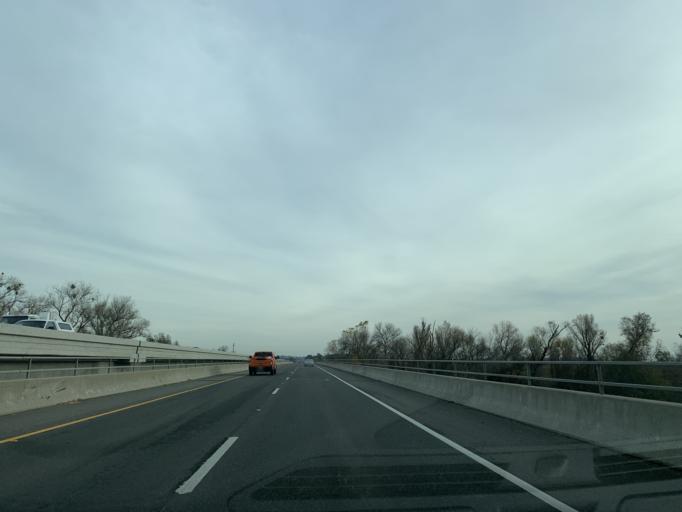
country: US
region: California
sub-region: Yuba County
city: Plumas Lake
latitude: 38.9013
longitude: -121.5869
